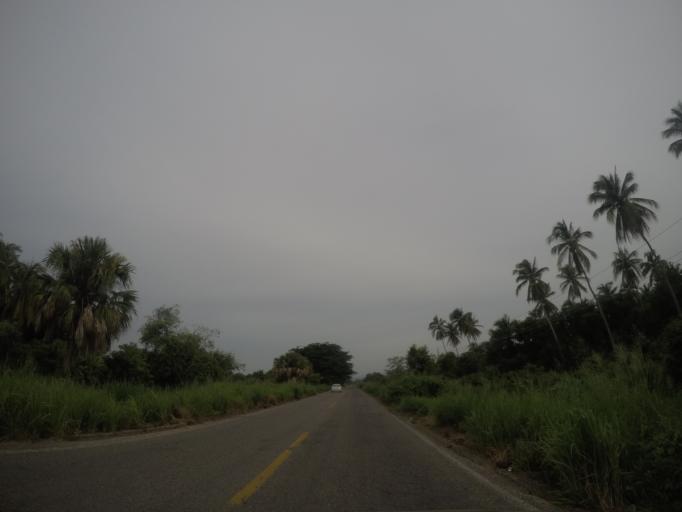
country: MX
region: Oaxaca
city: San Pedro Mixtepec
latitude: 15.9248
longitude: -97.1434
